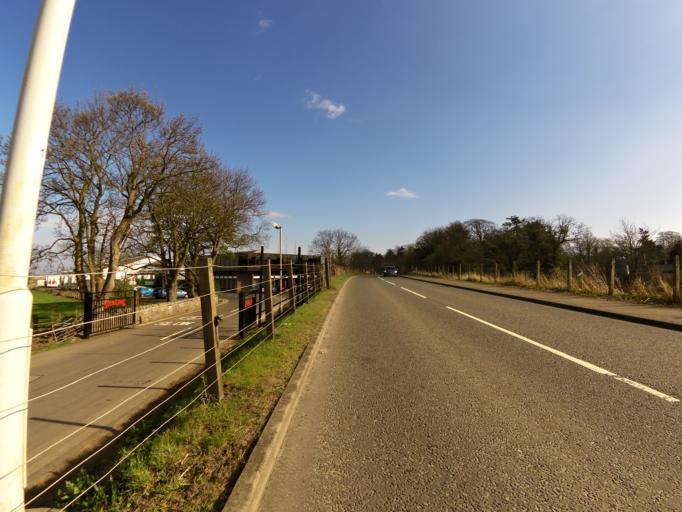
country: GB
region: Scotland
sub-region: Fife
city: Auchtermuchty
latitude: 56.2877
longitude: -3.2276
